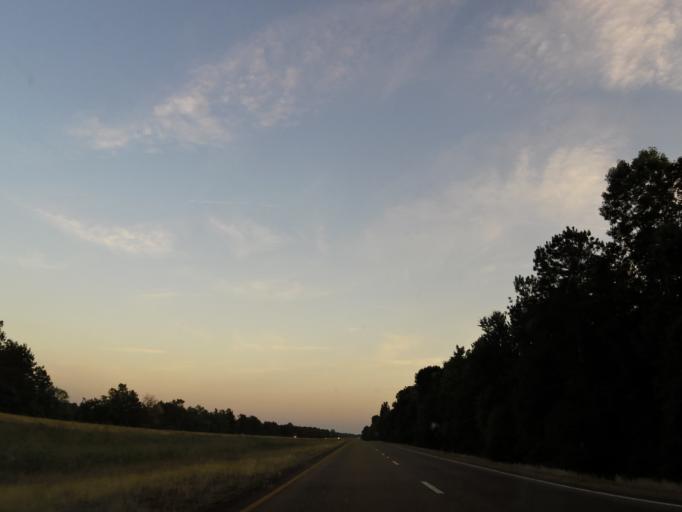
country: US
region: Mississippi
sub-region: Kemper County
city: De Kalb
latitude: 32.8605
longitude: -88.4821
